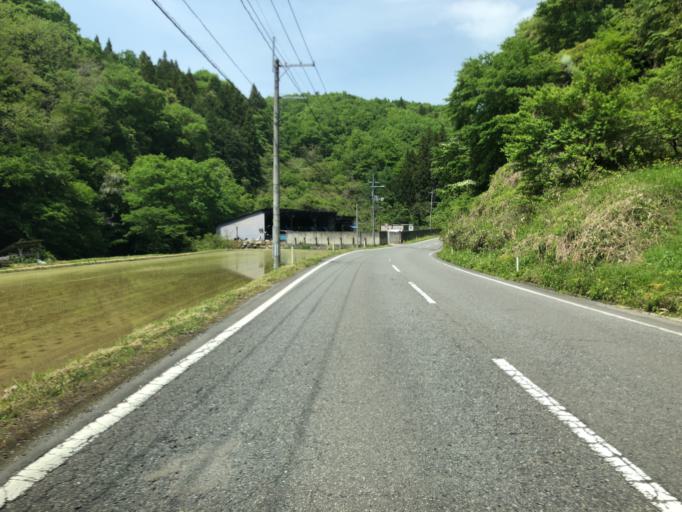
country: JP
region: Fukushima
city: Ishikawa
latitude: 37.1805
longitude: 140.4733
